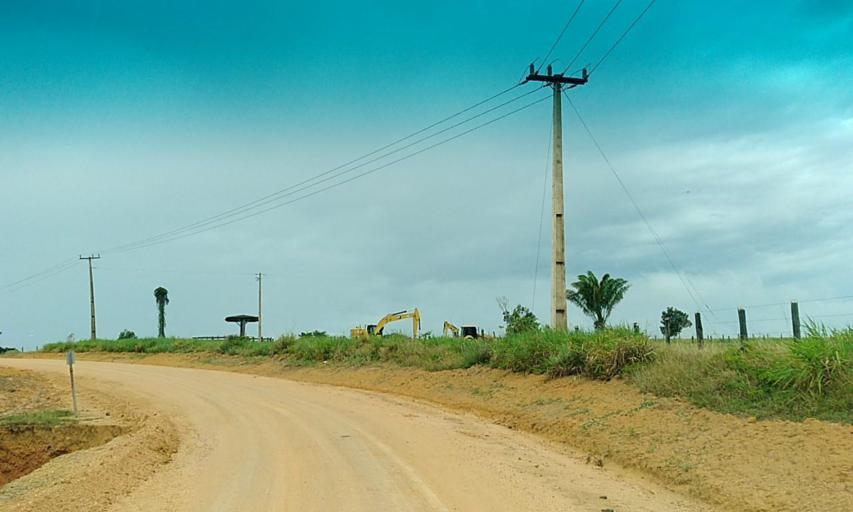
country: BR
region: Para
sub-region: Senador Jose Porfirio
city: Senador Jose Porfirio
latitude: -3.0584
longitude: -51.6723
